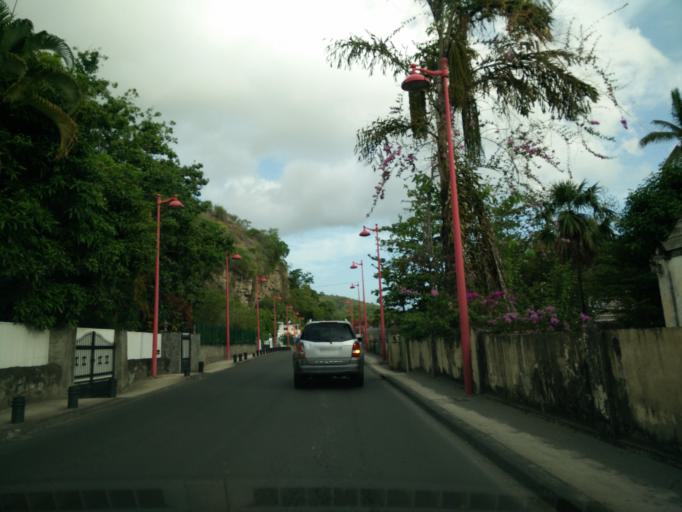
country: MQ
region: Martinique
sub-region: Martinique
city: Saint-Pierre
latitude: 14.7049
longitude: -61.1828
